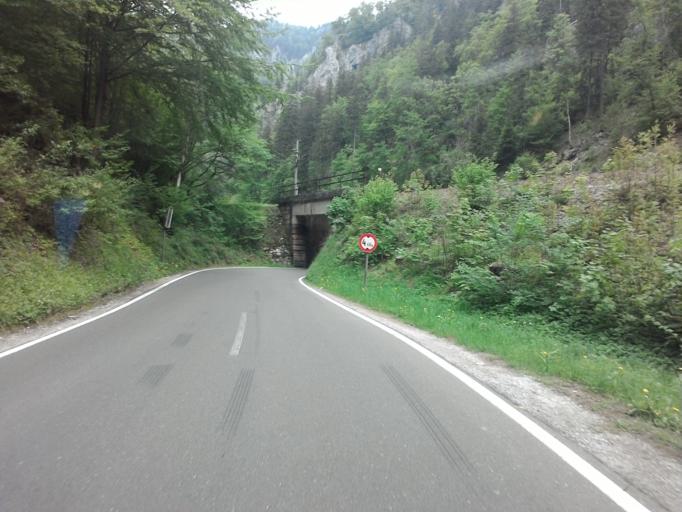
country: AT
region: Styria
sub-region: Politischer Bezirk Leoben
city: Eisenerz
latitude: 47.5784
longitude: 14.8274
